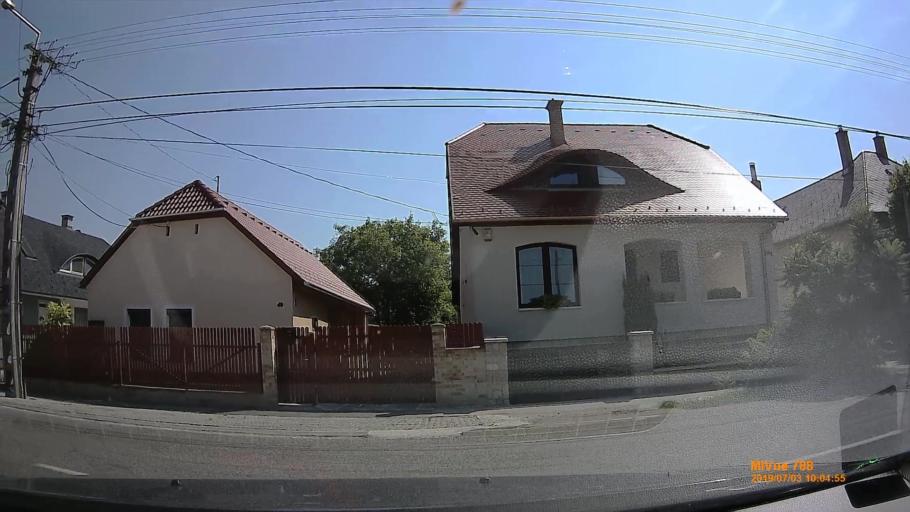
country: HU
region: Gyor-Moson-Sopron
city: Toltestava
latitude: 47.7025
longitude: 17.7288
